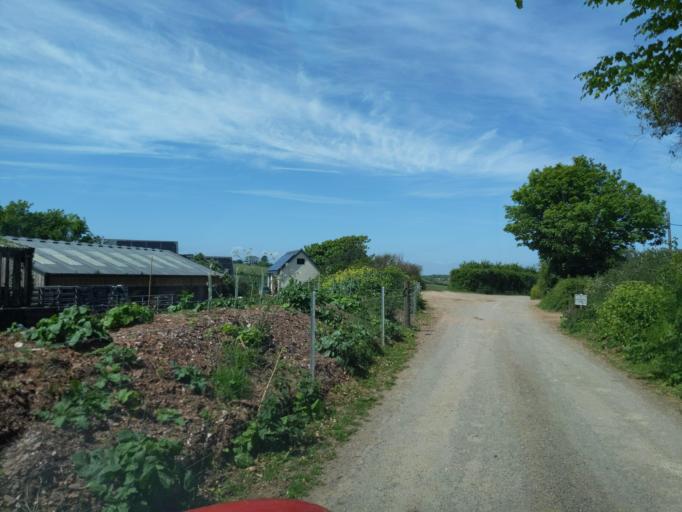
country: GB
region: England
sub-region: Borough of Torbay
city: Brixham
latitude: 50.3621
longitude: -3.5310
